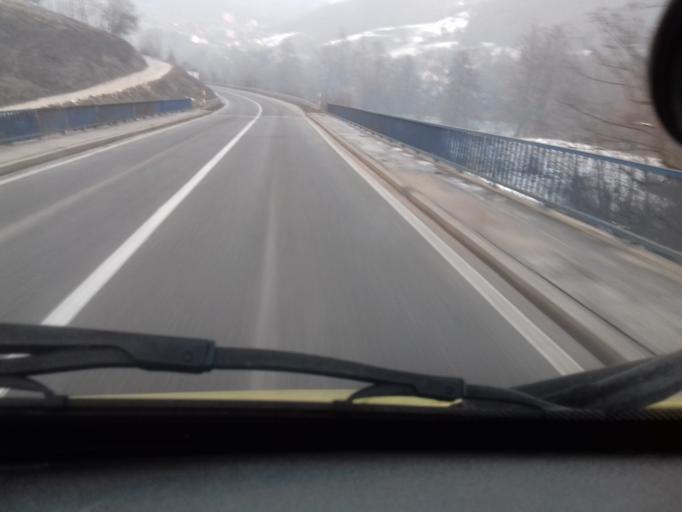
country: BA
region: Federation of Bosnia and Herzegovina
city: Vogosca
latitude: 43.8870
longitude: 18.3258
